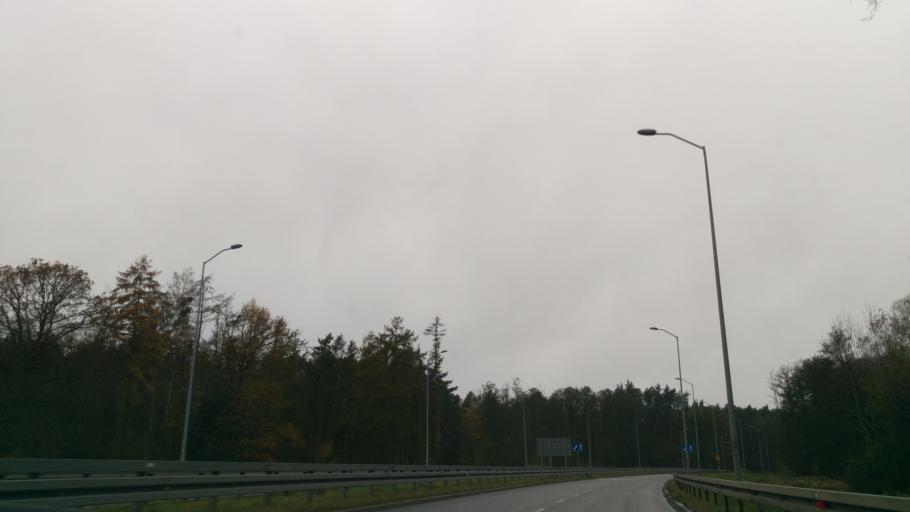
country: PL
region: West Pomeranian Voivodeship
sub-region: Powiat gryfinski
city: Stare Czarnowo
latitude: 53.3959
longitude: 14.7136
